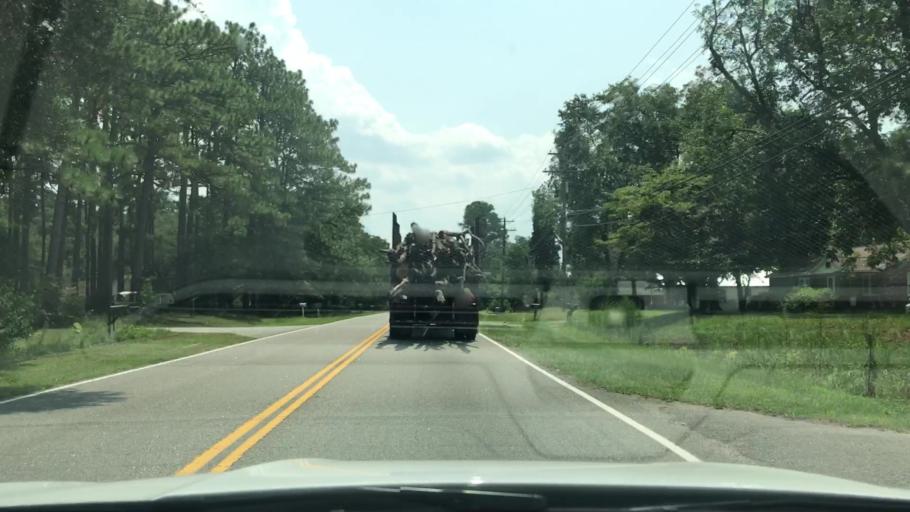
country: US
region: South Carolina
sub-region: Georgetown County
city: Georgetown
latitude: 33.4345
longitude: -79.2771
